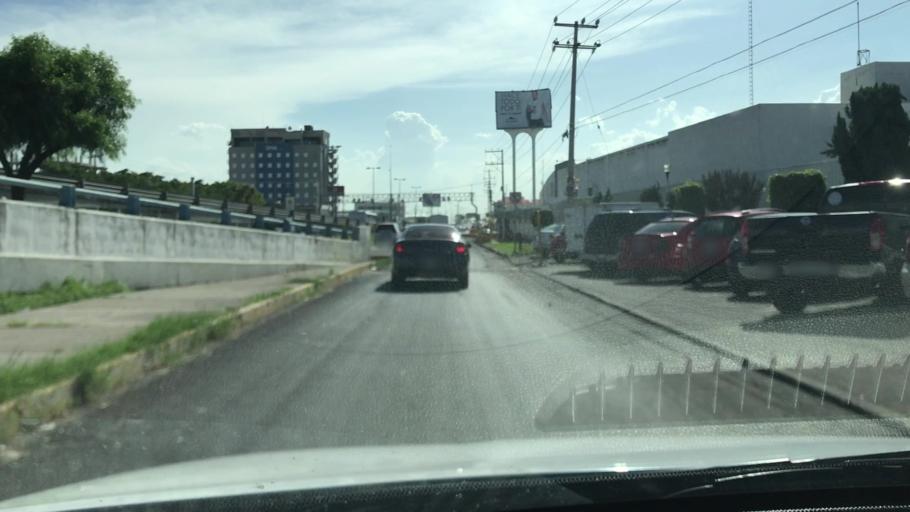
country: MX
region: Guanajuato
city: Celaya
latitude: 20.5194
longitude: -100.8409
